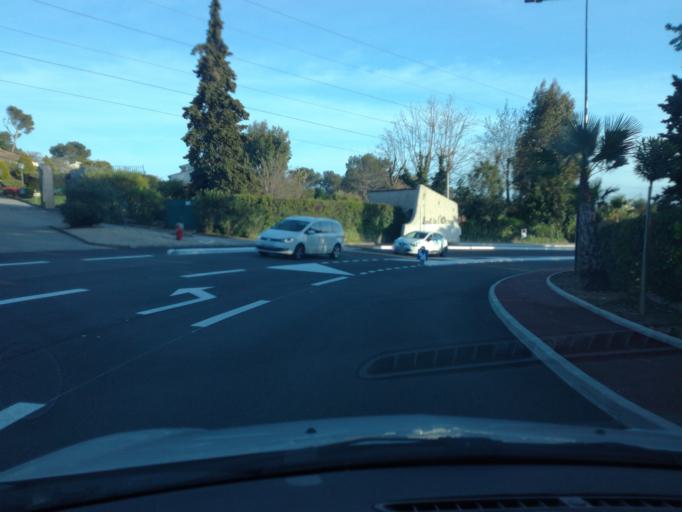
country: FR
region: Provence-Alpes-Cote d'Azur
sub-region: Departement des Alpes-Maritimes
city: Mougins
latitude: 43.6062
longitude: 7.0118
